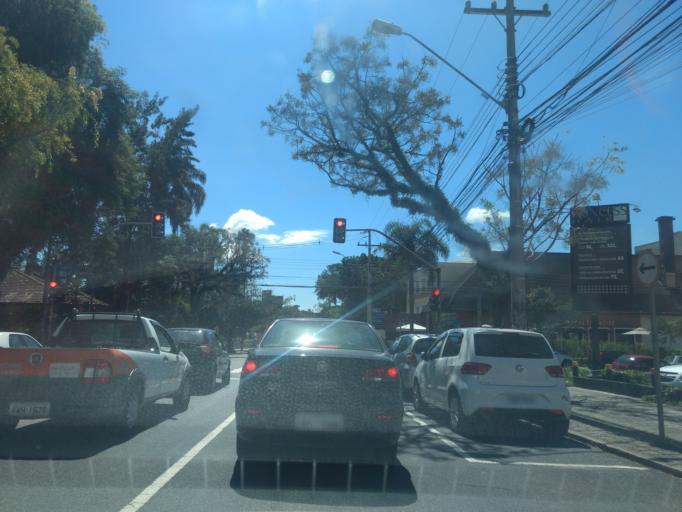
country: BR
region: Parana
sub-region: Curitiba
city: Curitiba
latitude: -25.4104
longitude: -49.2537
